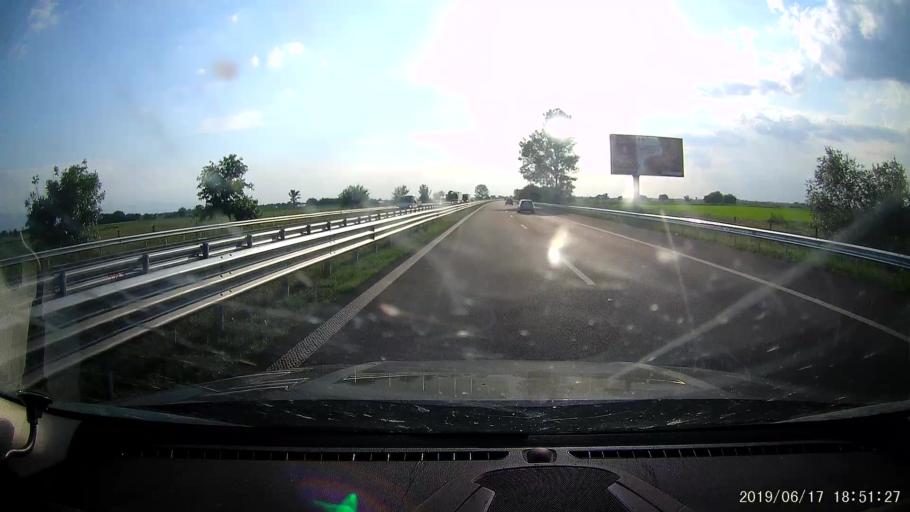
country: BG
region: Plovdiv
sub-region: Obshtina Rakovski
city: Rakovski
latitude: 42.2139
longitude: 24.9712
